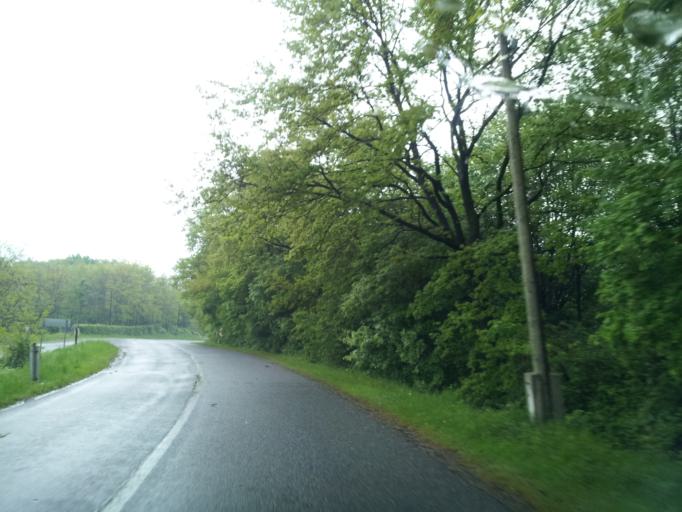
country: HU
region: Baranya
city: Hosszuheteny
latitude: 46.1800
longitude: 18.3189
